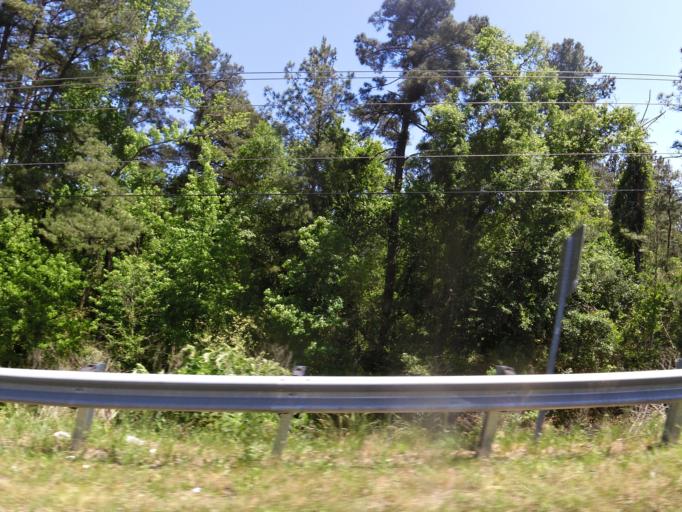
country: US
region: South Carolina
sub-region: Aiken County
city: Gloverville
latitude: 33.5358
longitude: -81.8357
